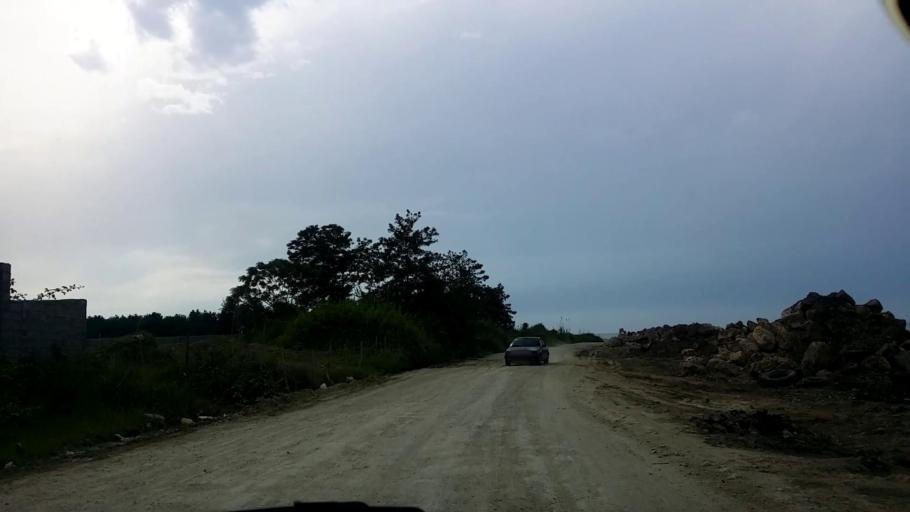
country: IR
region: Mazandaran
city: Chalus
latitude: 36.6842
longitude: 51.4298
